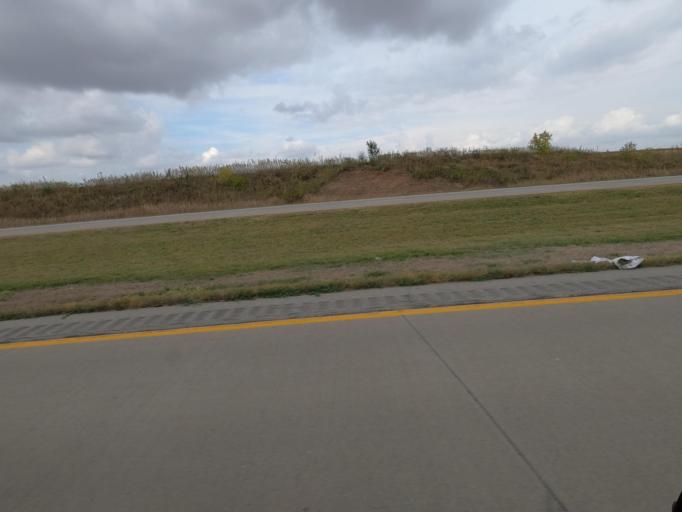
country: US
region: Iowa
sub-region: Jasper County
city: Prairie City
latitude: 41.5880
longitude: -93.2098
